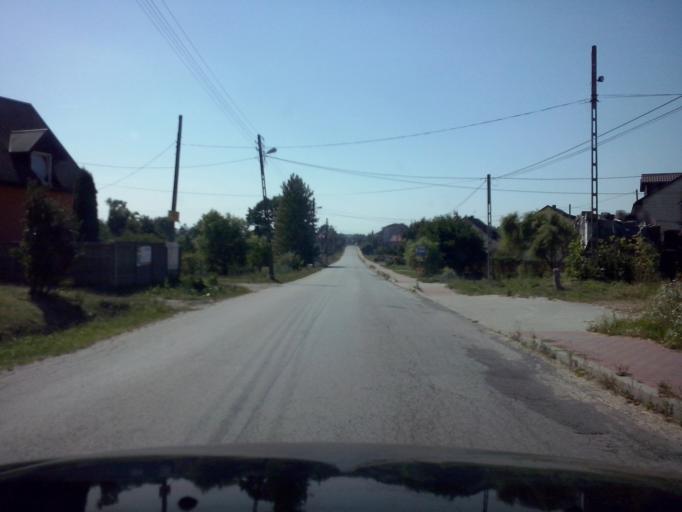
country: PL
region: Swietokrzyskie
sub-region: Powiat kielecki
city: Wola Jachowa
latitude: 50.8449
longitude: 20.8539
